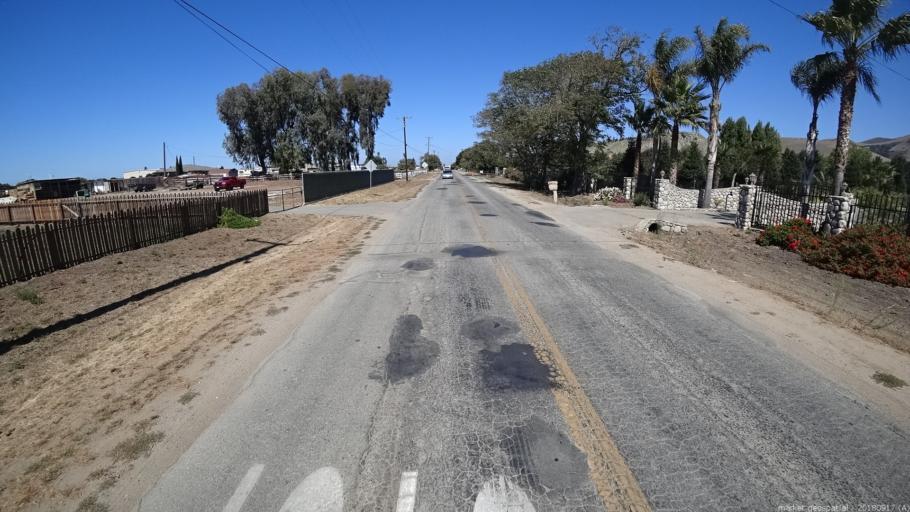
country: US
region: California
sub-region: Monterey County
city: Salinas
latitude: 36.7330
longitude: -121.5974
